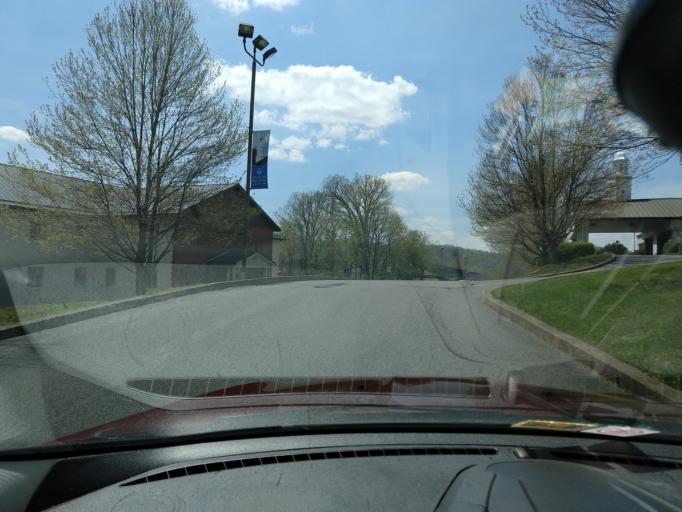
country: US
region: West Virginia
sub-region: Raleigh County
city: Bradley
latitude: 37.8529
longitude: -81.1982
